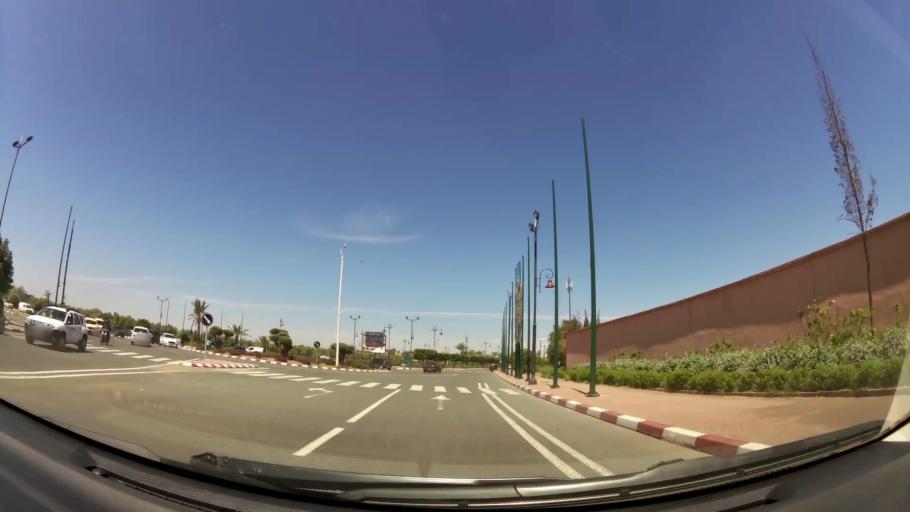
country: MA
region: Marrakech-Tensift-Al Haouz
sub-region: Marrakech
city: Marrakesh
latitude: 31.6148
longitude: -7.9950
